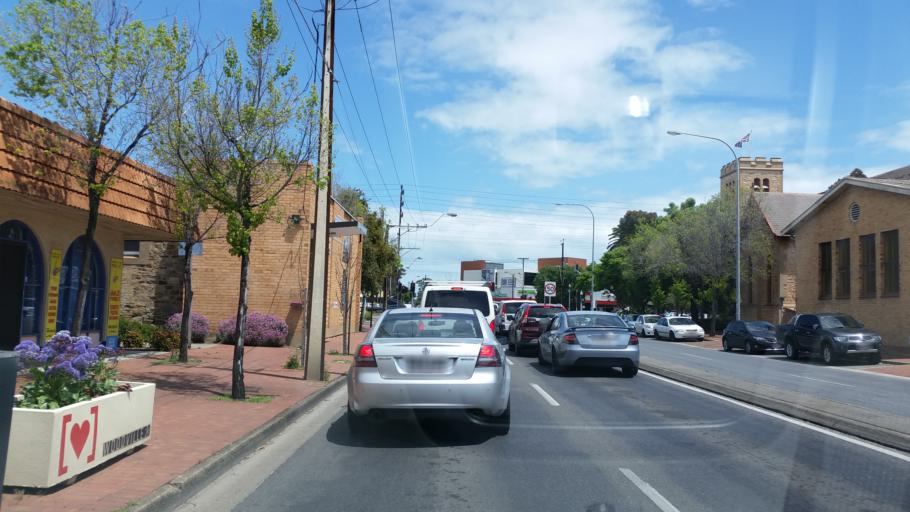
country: AU
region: South Australia
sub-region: Charles Sturt
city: Woodville West
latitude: -34.8799
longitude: 138.5360
